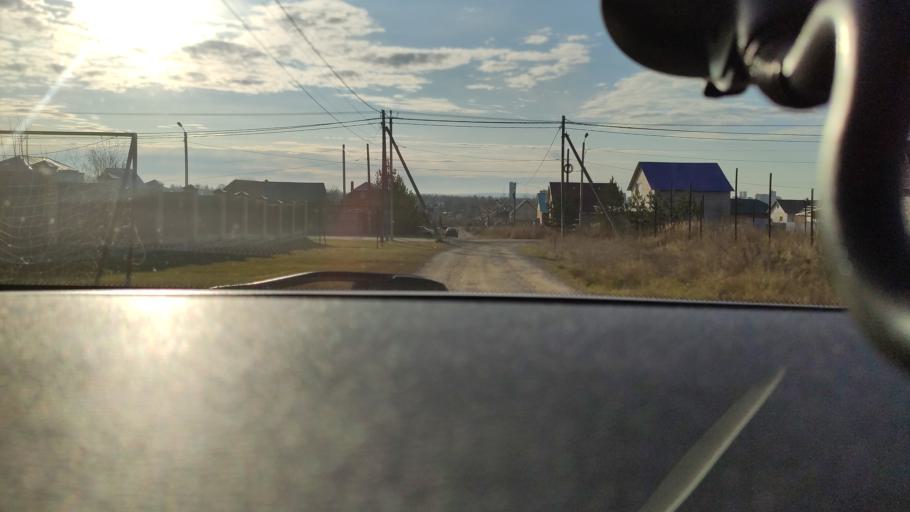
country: RU
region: Perm
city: Kondratovo
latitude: 58.0591
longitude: 56.0368
